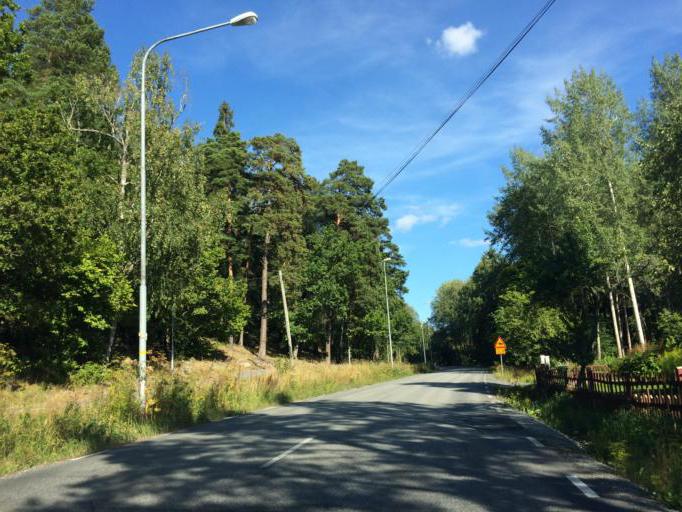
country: SE
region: Stockholm
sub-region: Upplands Vasby Kommun
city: Upplands Vaesby
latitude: 59.4868
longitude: 17.9366
